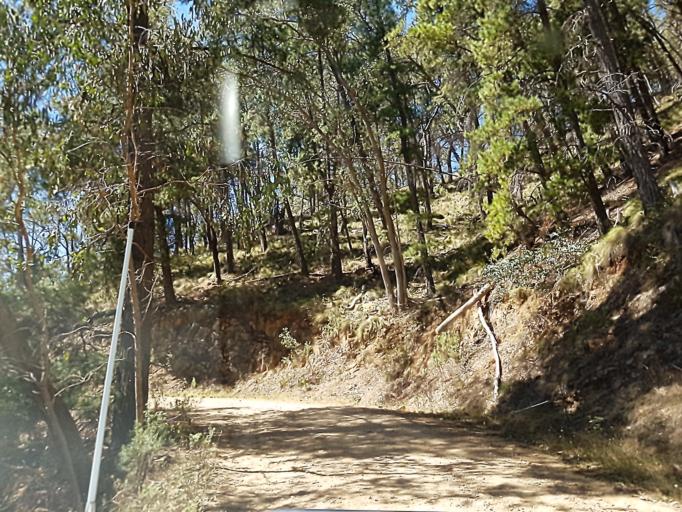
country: AU
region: Victoria
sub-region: Alpine
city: Mount Beauty
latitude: -36.7405
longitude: 146.9623
